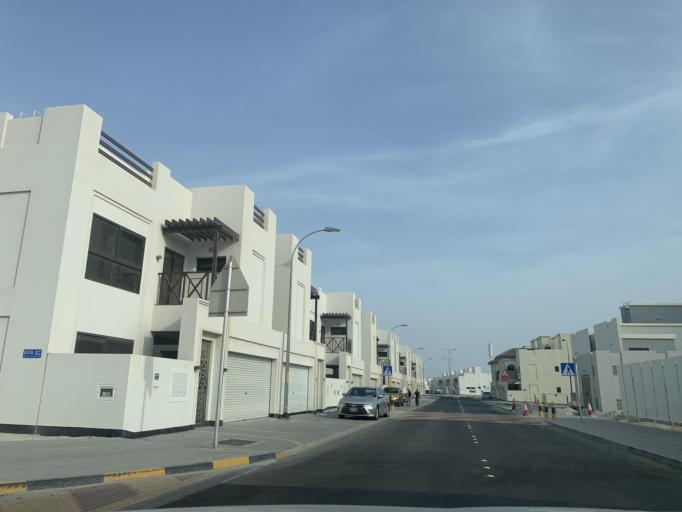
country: BH
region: Muharraq
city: Al Muharraq
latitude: 26.3162
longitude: 50.6287
